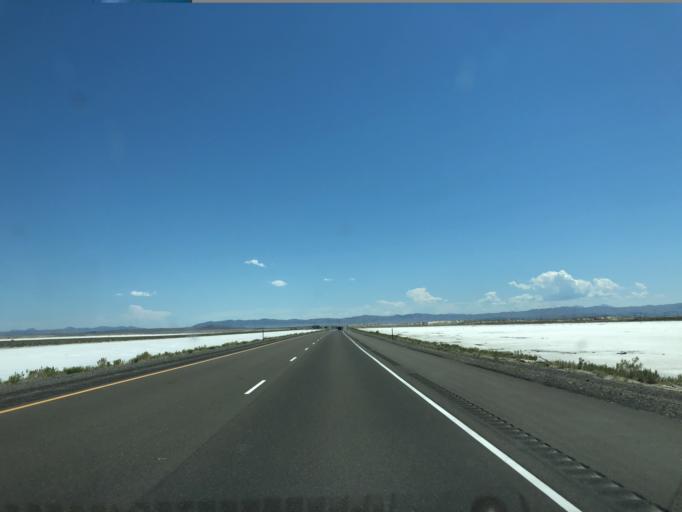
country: US
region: Utah
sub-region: Tooele County
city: Wendover
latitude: 40.7272
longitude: -113.2981
